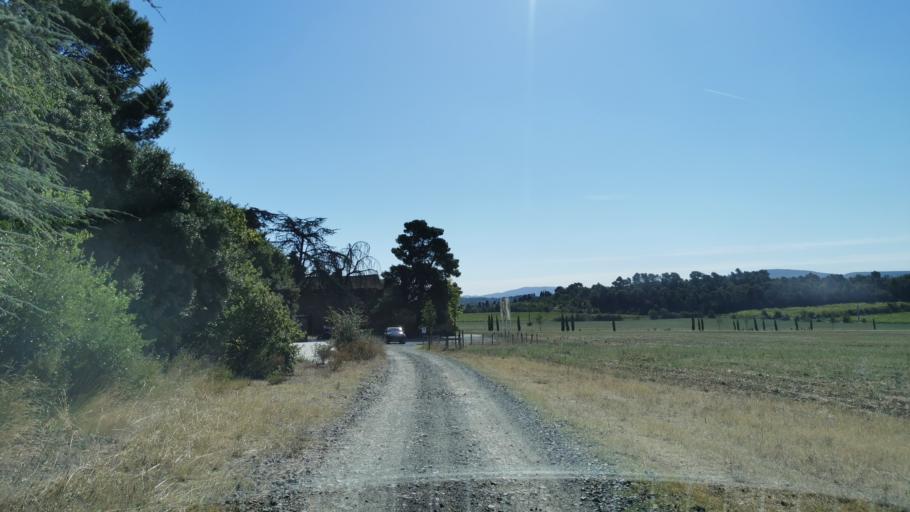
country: FR
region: Languedoc-Roussillon
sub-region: Departement de l'Aude
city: Conques-sur-Orbiel
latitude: 43.2433
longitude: 2.4158
